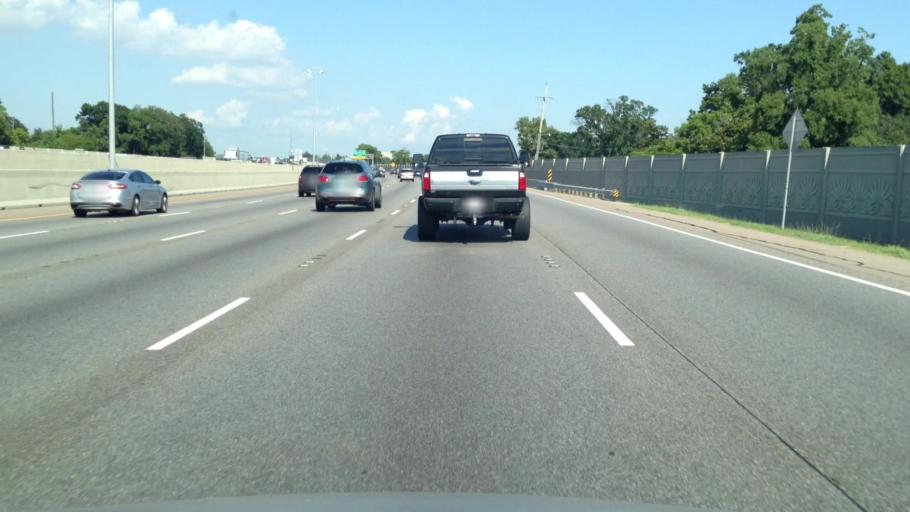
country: US
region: Louisiana
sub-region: Jefferson Parish
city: Kenner
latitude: 30.0005
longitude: -90.2002
